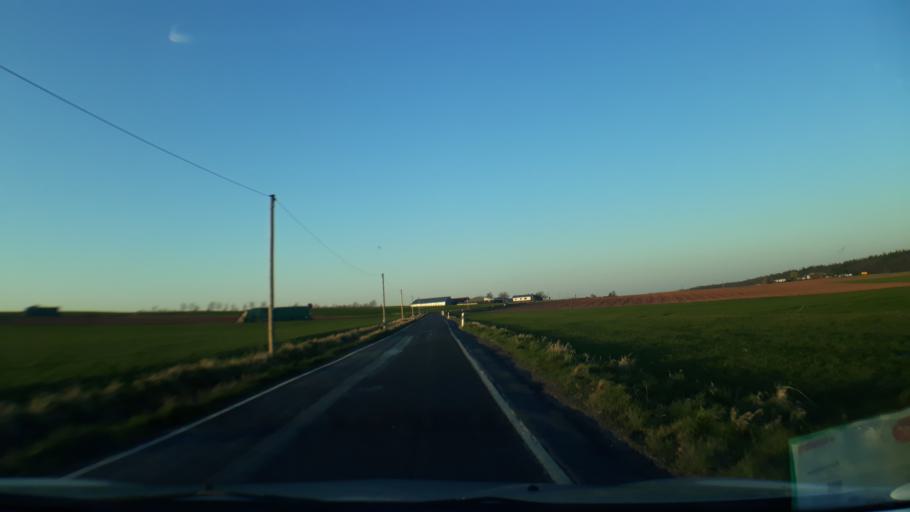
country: DE
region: North Rhine-Westphalia
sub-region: Regierungsbezirk Koln
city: Mechernich
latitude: 50.6120
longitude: 6.5973
